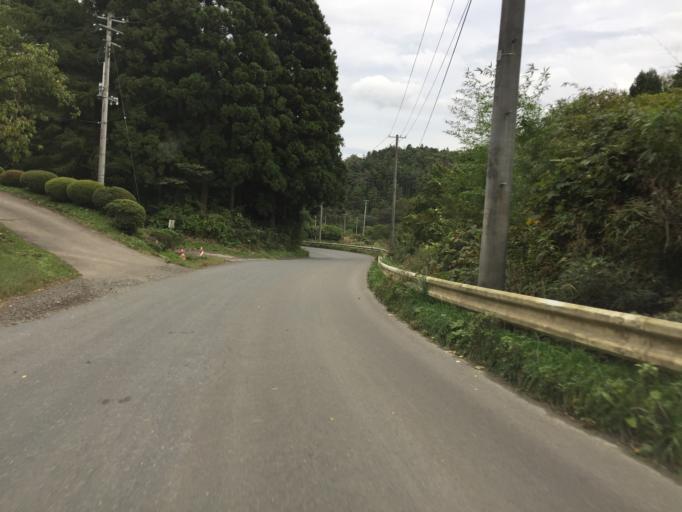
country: JP
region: Miyagi
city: Marumori
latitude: 37.8989
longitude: 140.7287
